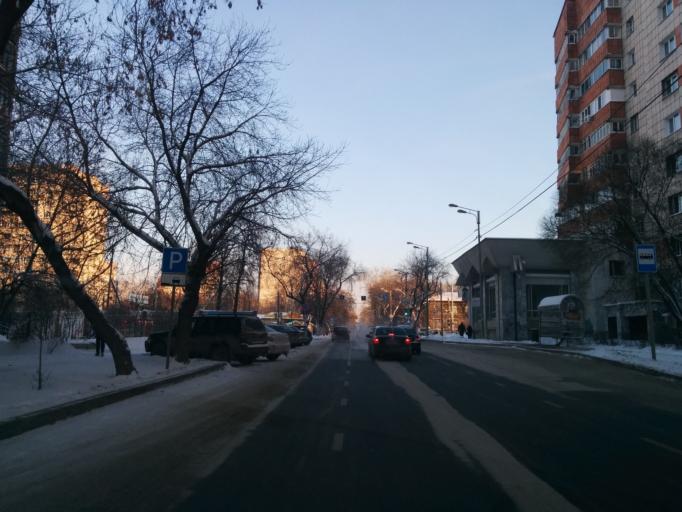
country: RU
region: Perm
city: Perm
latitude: 58.0038
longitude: 56.2208
